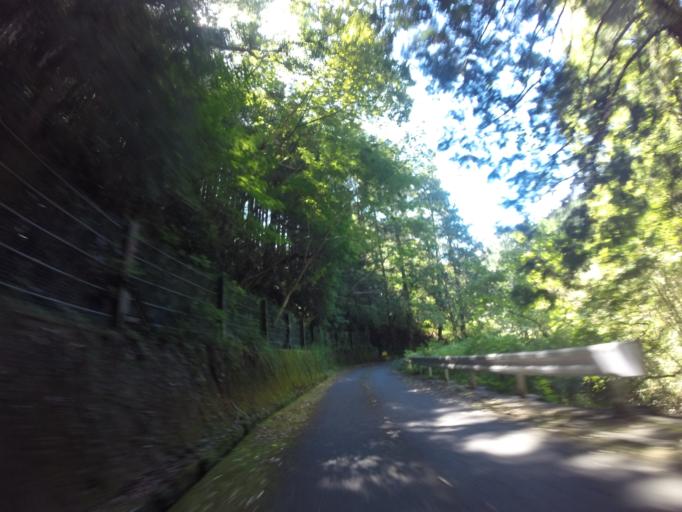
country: JP
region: Shizuoka
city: Kanaya
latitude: 34.8972
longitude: 138.1531
